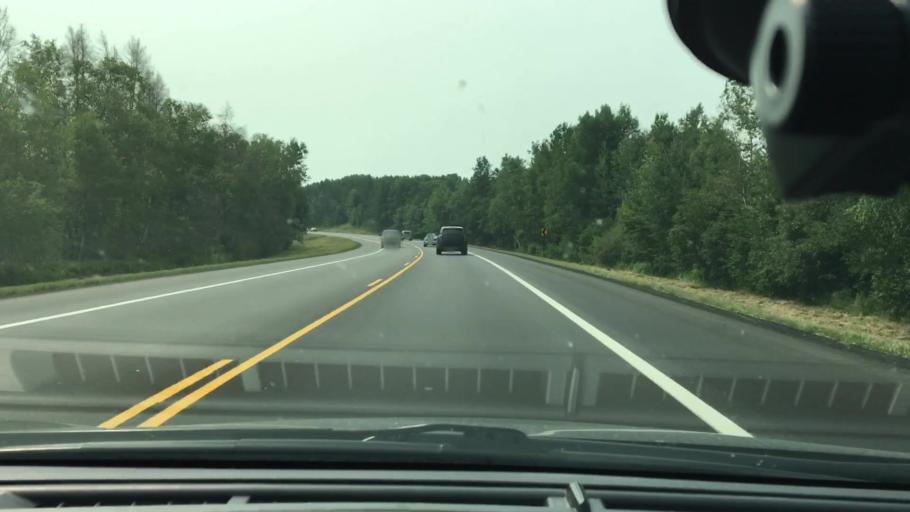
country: US
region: Minnesota
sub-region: Crow Wing County
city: Brainerd
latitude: 46.4191
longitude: -94.1788
